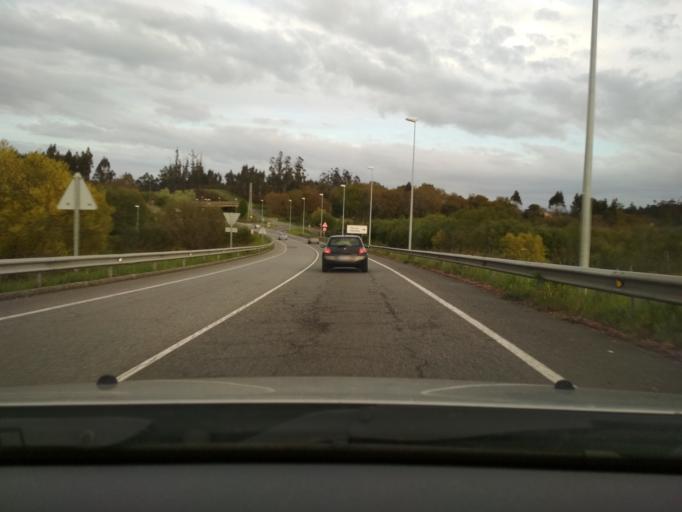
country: ES
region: Galicia
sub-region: Provincia da Coruna
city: Santiago de Compostela
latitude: 42.8981
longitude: -8.5250
